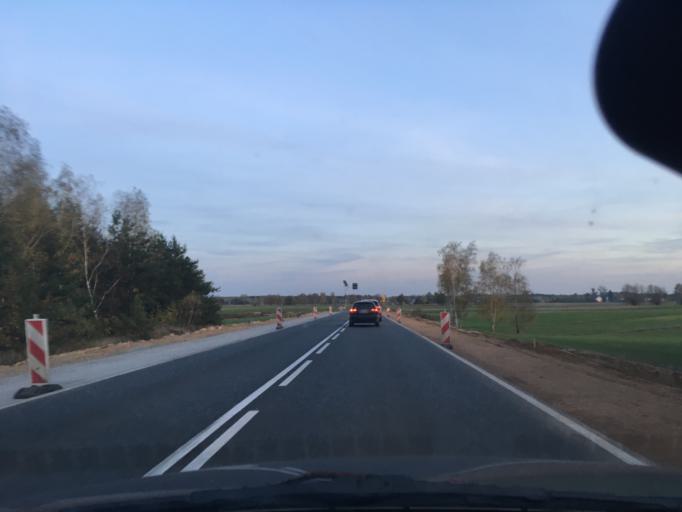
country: PL
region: Masovian Voivodeship
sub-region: Powiat plocki
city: Wyszogrod
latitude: 52.3618
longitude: 20.1987
